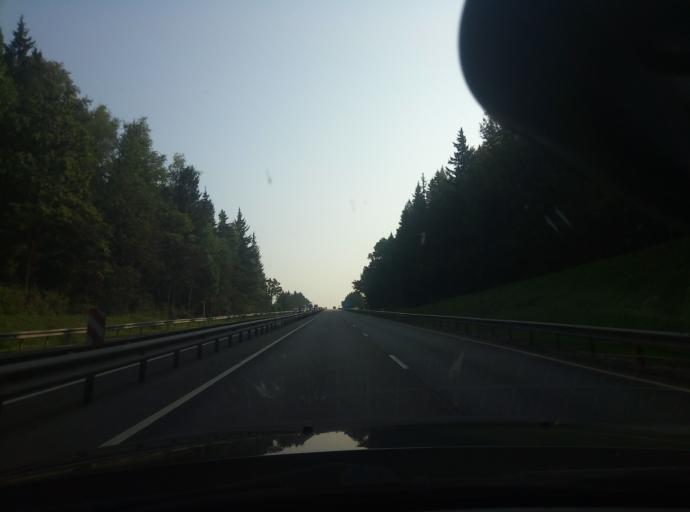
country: RU
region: Kaluga
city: Maloyaroslavets
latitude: 55.0033
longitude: 36.5329
